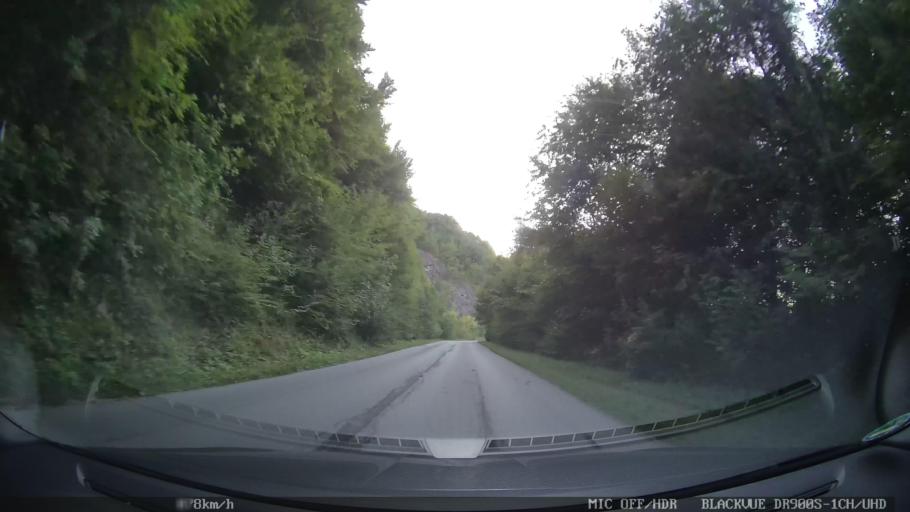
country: HR
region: Karlovacka
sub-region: Grad Ogulin
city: Ogulin
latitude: 45.2689
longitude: 15.1838
